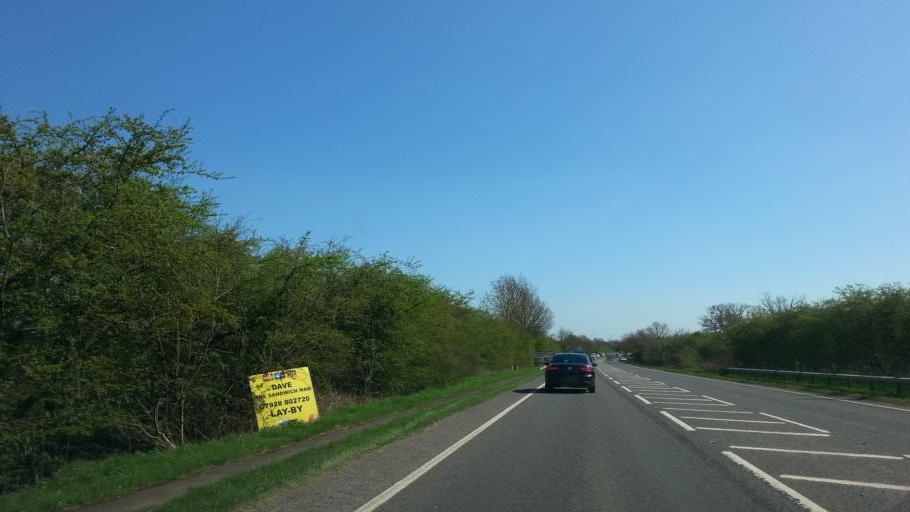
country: GB
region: England
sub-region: Worcestershire
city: Alvechurch
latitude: 52.3670
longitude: -1.9530
